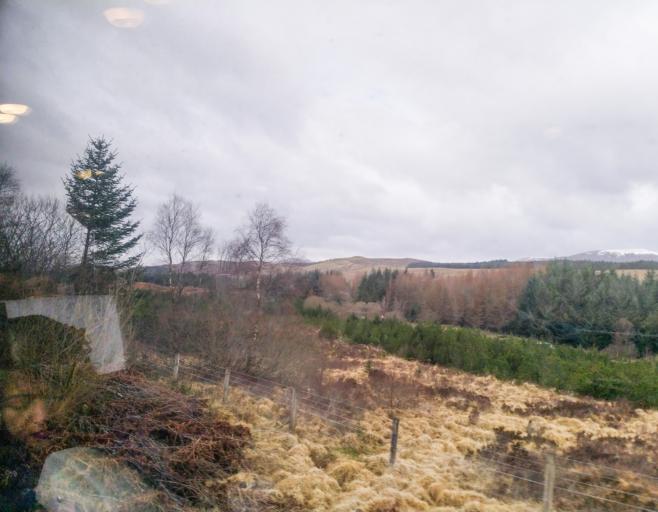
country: GB
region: Scotland
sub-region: Highland
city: Spean Bridge
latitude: 56.8807
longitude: -4.9618
